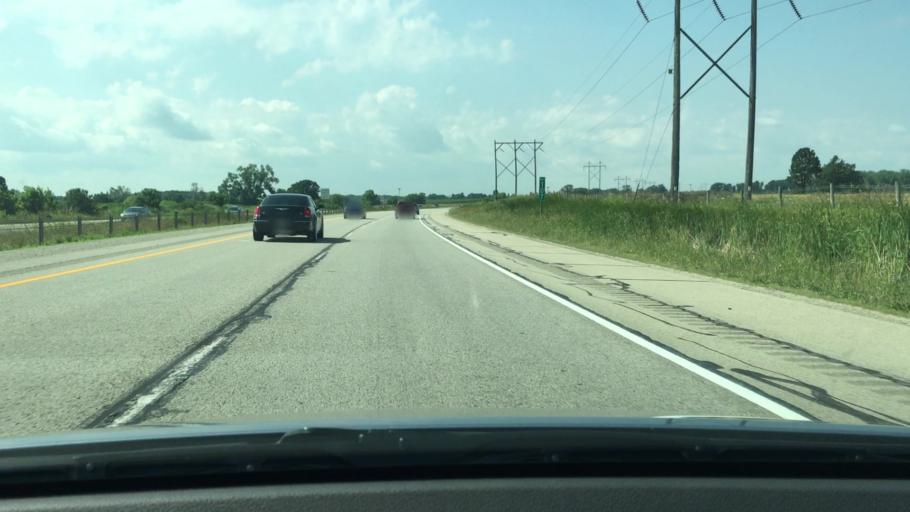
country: US
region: Wisconsin
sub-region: Fond du Lac County
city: Rosendale
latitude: 43.8579
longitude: -88.5810
